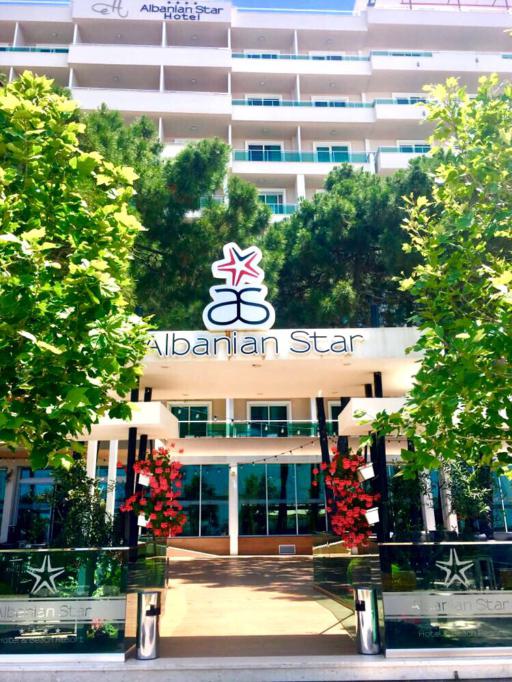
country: AL
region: Tirane
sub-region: Rrethi i Kavajes
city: Golem
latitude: 41.2604
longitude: 19.5202
